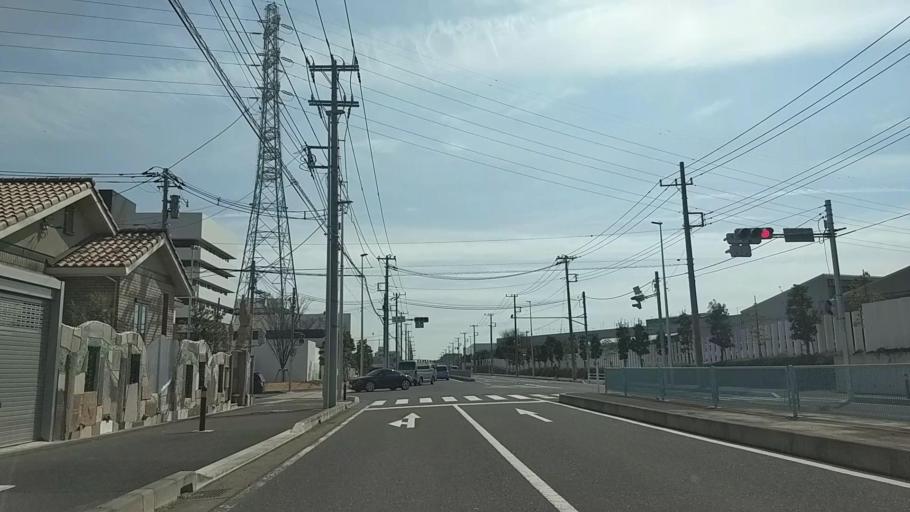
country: JP
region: Kanagawa
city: Fujisawa
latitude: 35.4006
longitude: 139.4559
